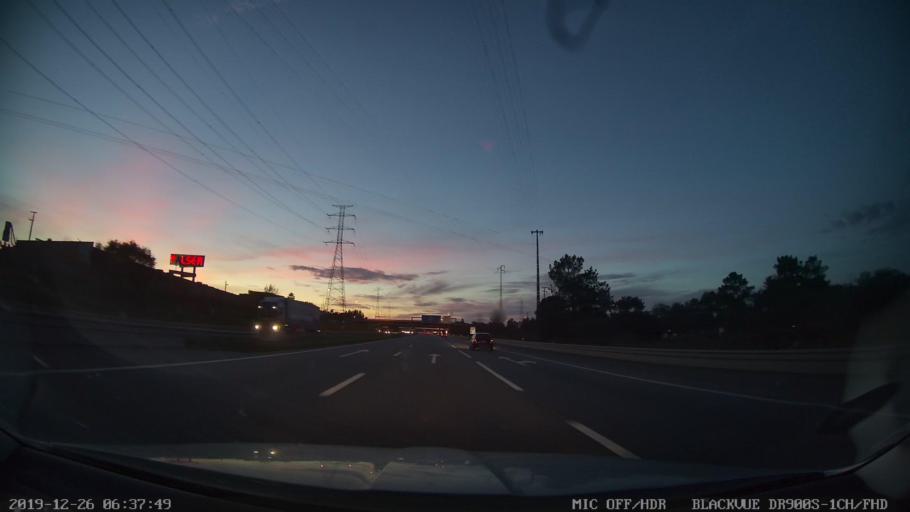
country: PT
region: Setubal
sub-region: Palmela
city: Palmela
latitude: 38.5834
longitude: -8.8841
